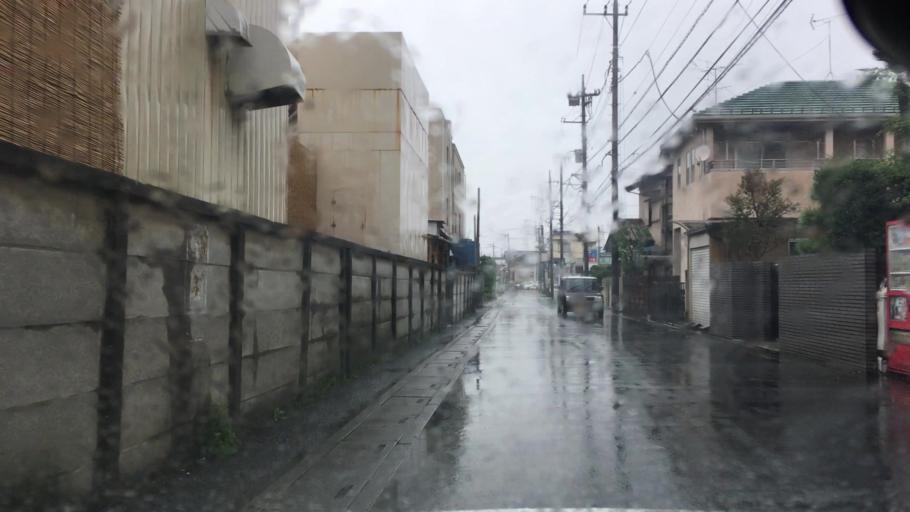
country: JP
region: Saitama
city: Yono
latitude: 35.9062
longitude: 139.5995
